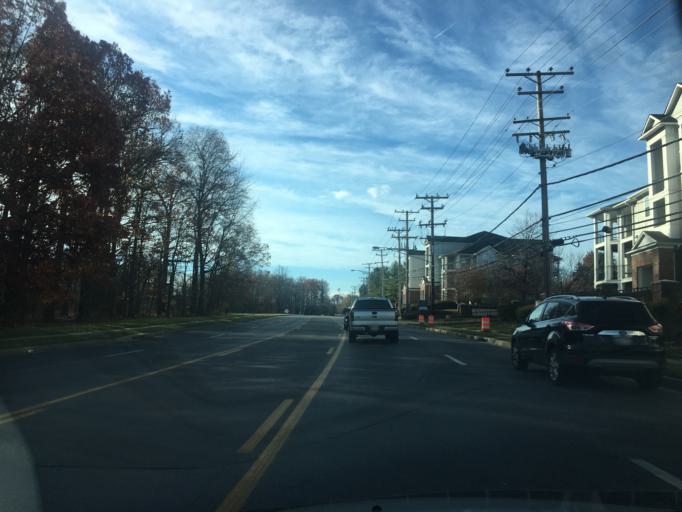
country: US
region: Maryland
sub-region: Baltimore County
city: Owings Mills
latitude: 39.4003
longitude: -76.7851
